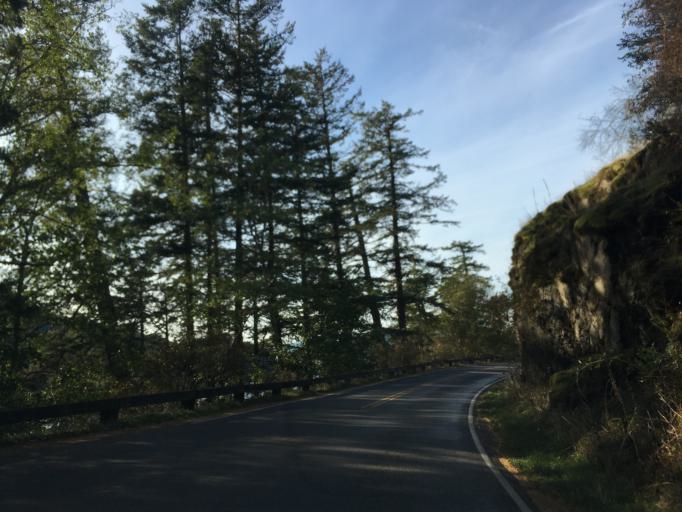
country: US
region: Washington
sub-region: San Juan County
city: Friday Harbor
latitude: 48.6491
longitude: -122.8472
